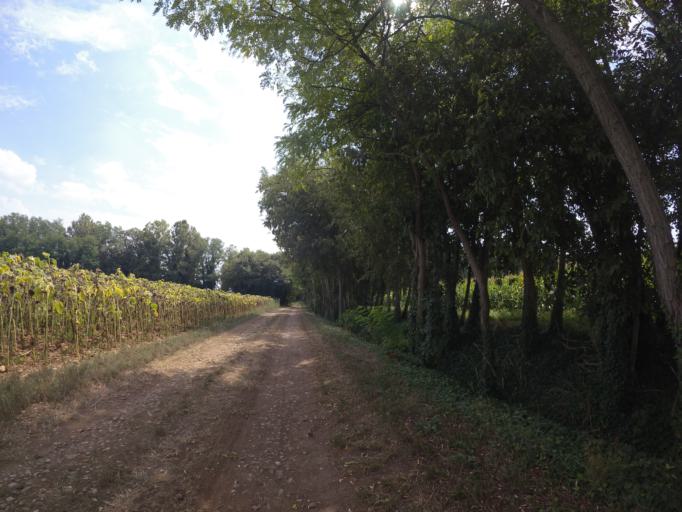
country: IT
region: Friuli Venezia Giulia
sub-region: Provincia di Udine
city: Bertiolo
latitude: 45.9579
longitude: 13.0696
